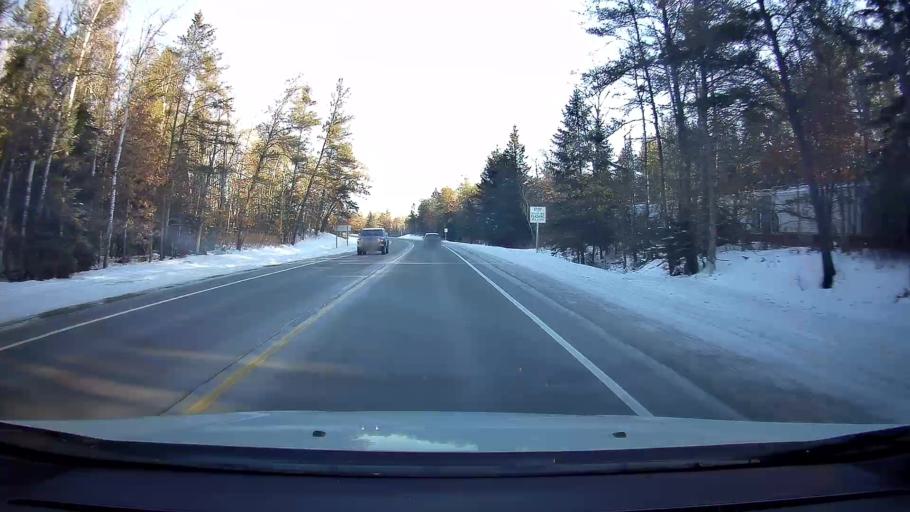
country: US
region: Wisconsin
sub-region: Sawyer County
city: Hayward
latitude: 45.9493
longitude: -91.6868
